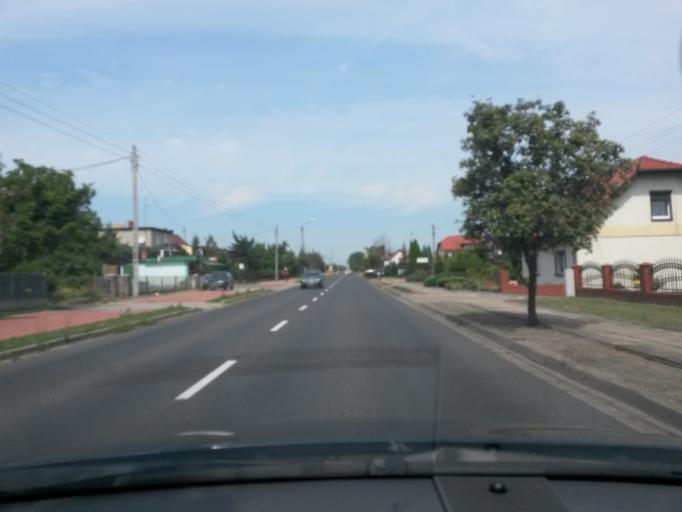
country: PL
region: Greater Poland Voivodeship
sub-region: Powiat gostynski
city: Gostyn
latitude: 51.8991
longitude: 17.0104
